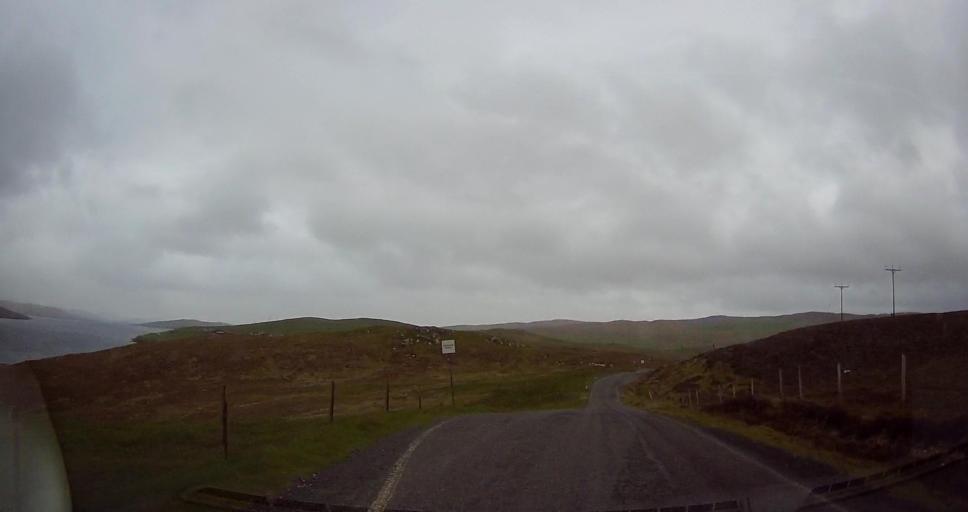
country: GB
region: Scotland
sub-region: Shetland Islands
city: Lerwick
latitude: 60.3807
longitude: -1.3794
